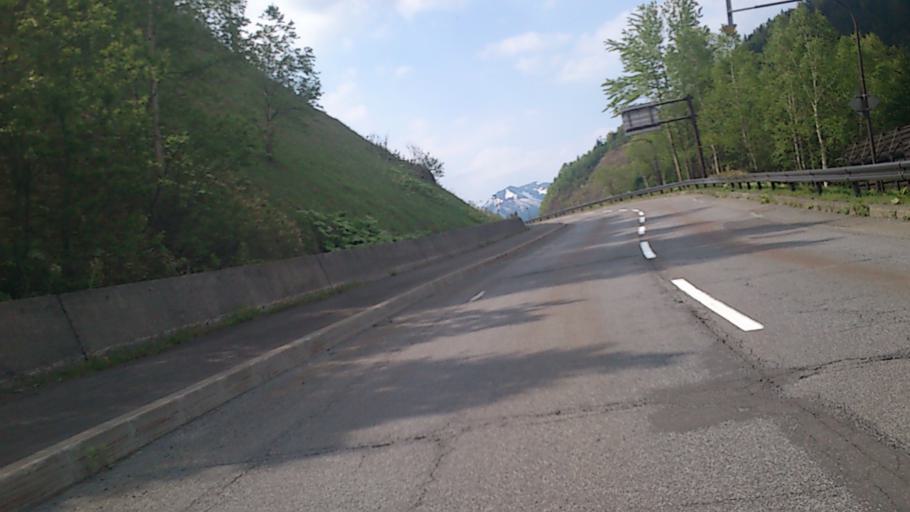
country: JP
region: Hokkaido
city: Kamikawa
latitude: 43.6800
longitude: 143.0373
